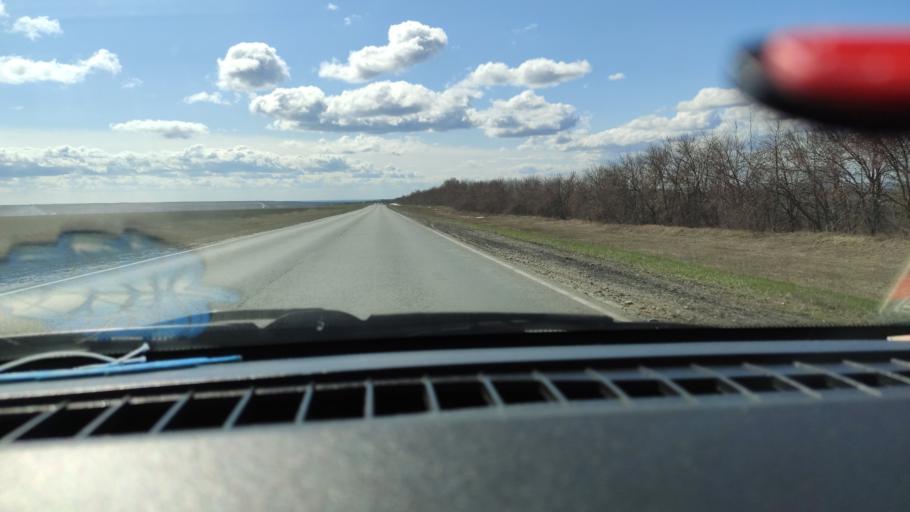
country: RU
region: Saratov
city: Dukhovnitskoye
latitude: 52.7726
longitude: 48.2360
